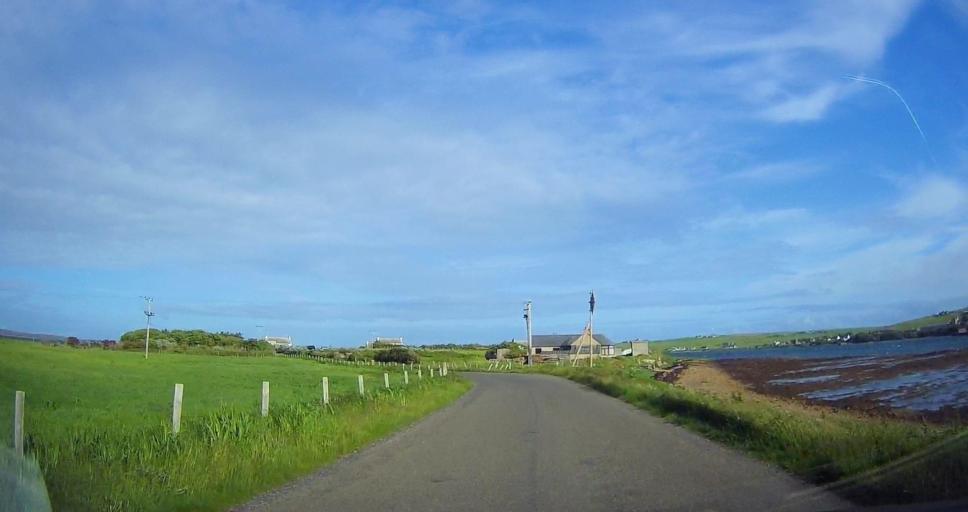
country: GB
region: Scotland
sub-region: Orkney Islands
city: Stromness
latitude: 58.8069
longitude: -3.2089
